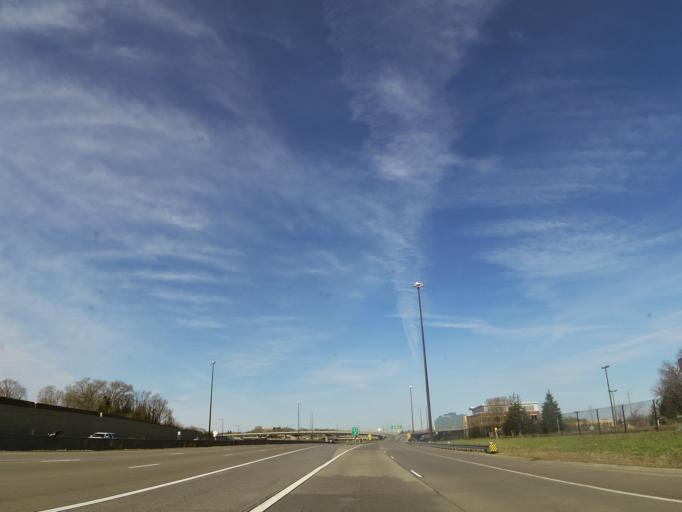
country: US
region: Minnesota
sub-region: Hennepin County
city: Edina
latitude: 44.8600
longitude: -93.3870
